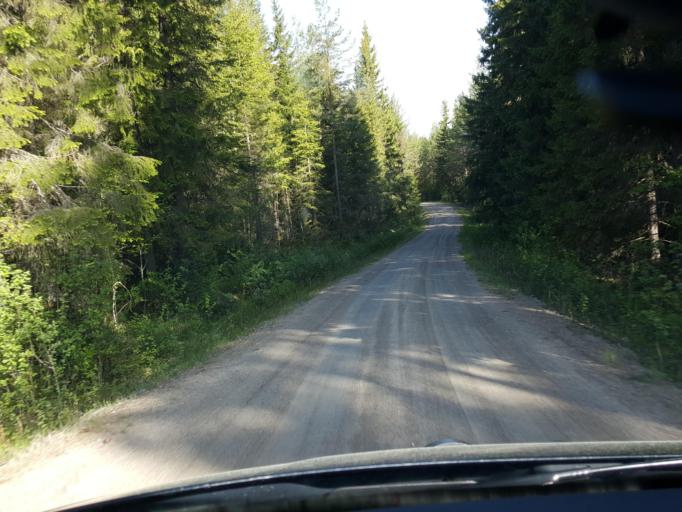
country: SE
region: Vaesternorrland
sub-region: Ange Kommun
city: Ange
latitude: 62.1799
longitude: 15.6253
